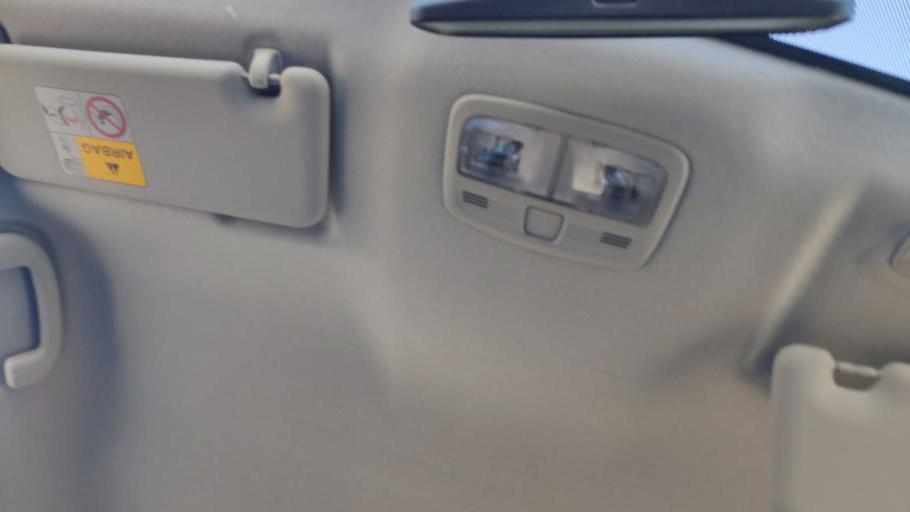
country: RS
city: Ostruznica
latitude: 44.7422
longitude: 20.2735
